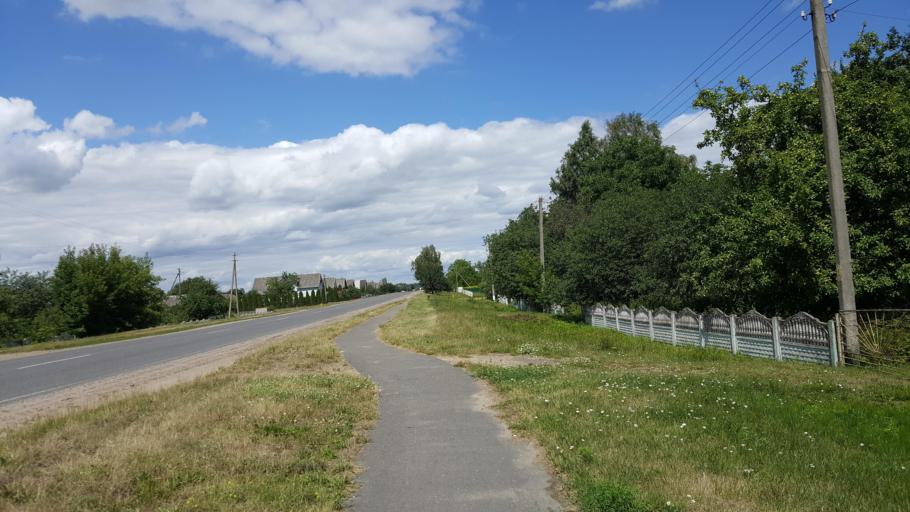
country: BY
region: Brest
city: Kamyanyets
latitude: 52.3191
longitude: 23.9193
